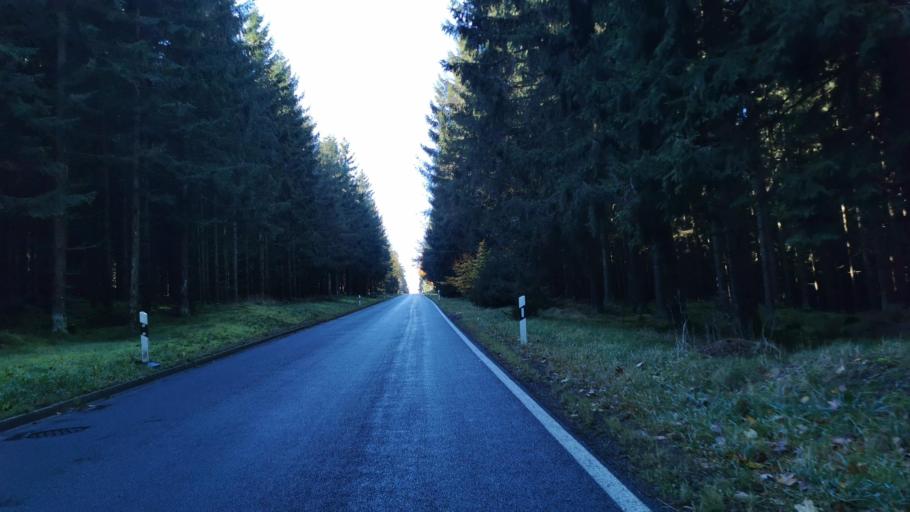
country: DE
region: Thuringia
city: Wurzbach
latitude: 50.4392
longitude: 11.5164
